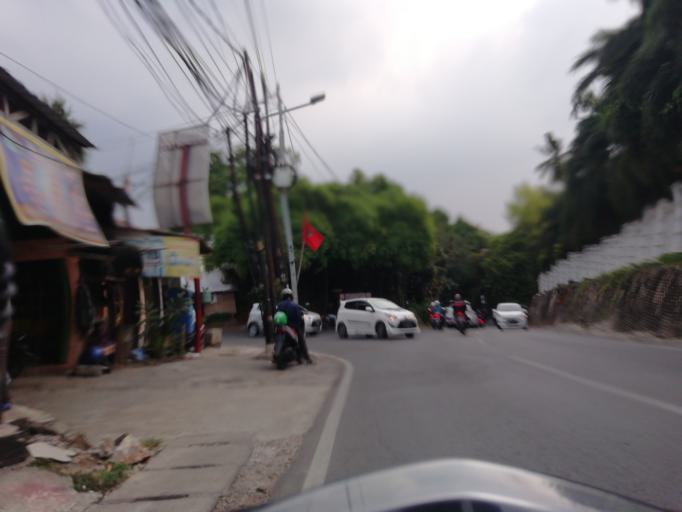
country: ID
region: West Java
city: Depok
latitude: -6.3268
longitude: 106.8110
